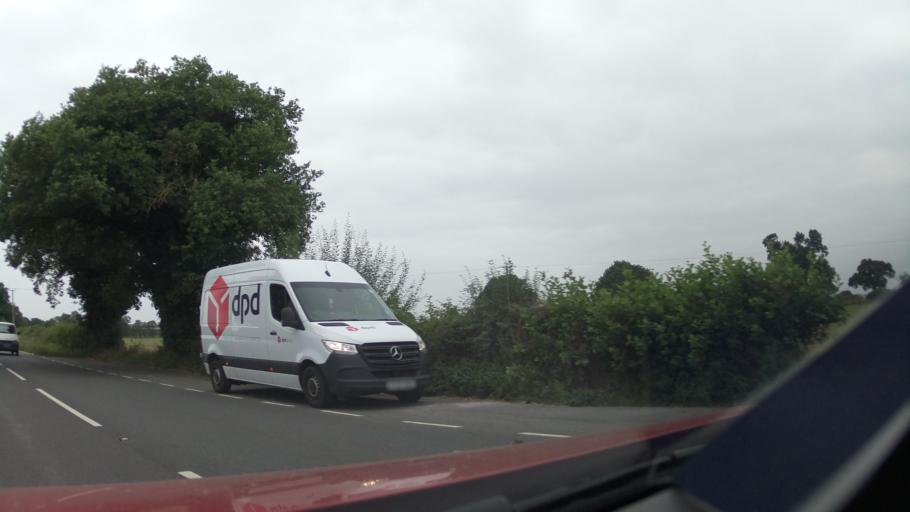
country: GB
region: England
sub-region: Shropshire
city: Shawbury
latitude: 52.8119
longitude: -2.6145
